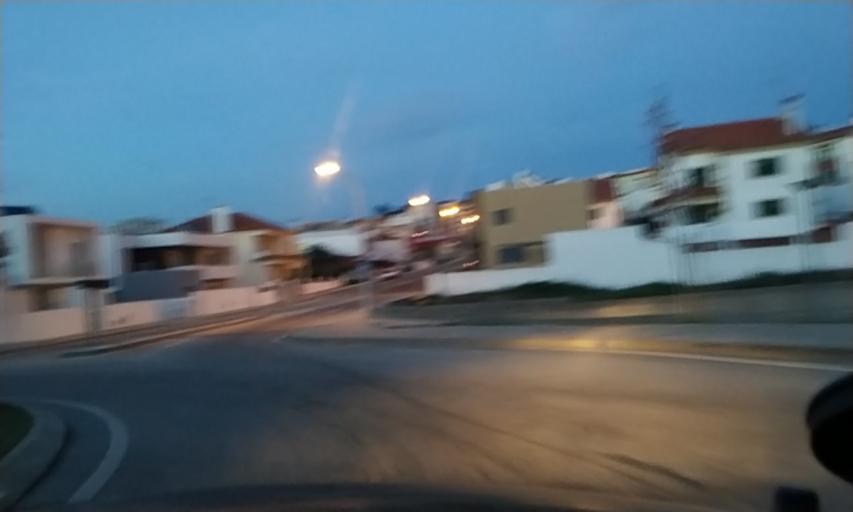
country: PT
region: Castelo Branco
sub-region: Castelo Branco
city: Castelo Branco
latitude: 39.8216
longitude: -7.5079
